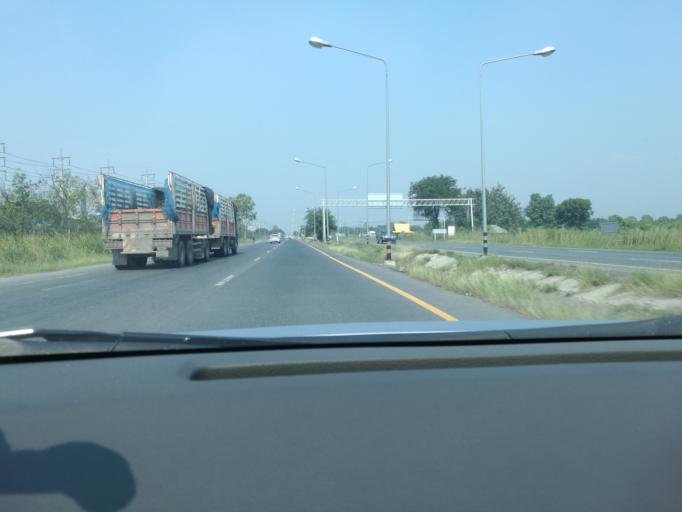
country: TH
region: Sara Buri
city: Saraburi
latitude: 14.5640
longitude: 100.9044
